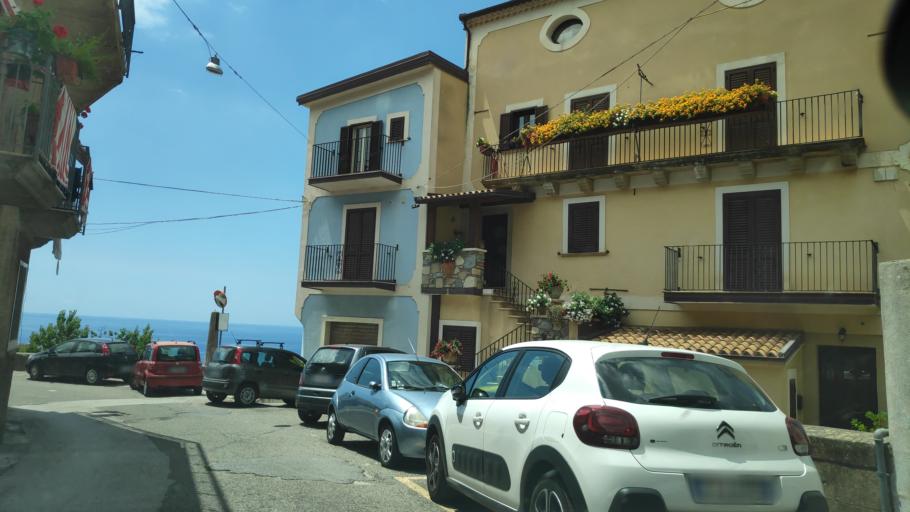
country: IT
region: Calabria
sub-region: Provincia di Cosenza
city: Paola
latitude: 39.3593
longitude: 16.0438
